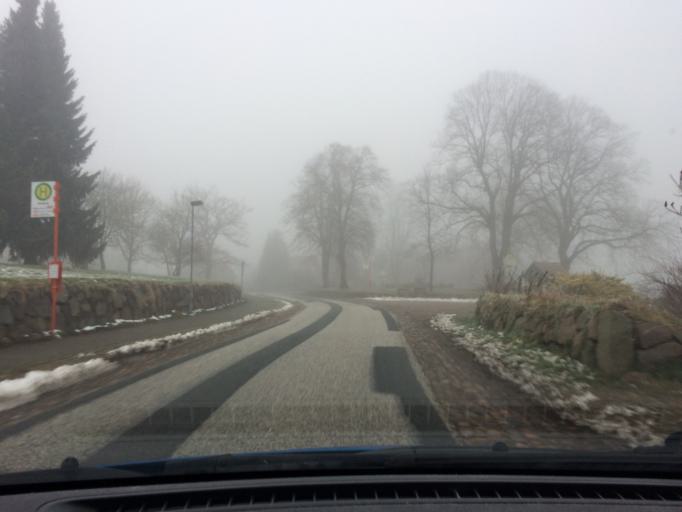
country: DE
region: Schleswig-Holstein
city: Juliusburg
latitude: 53.4163
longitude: 10.5058
